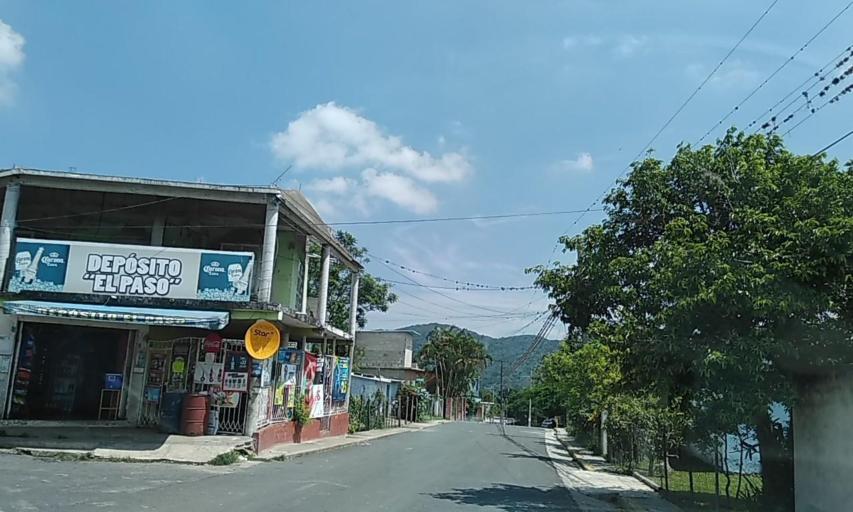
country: MX
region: Veracruz
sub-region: Emiliano Zapata
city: Dos Rios
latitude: 19.4372
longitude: -96.7784
